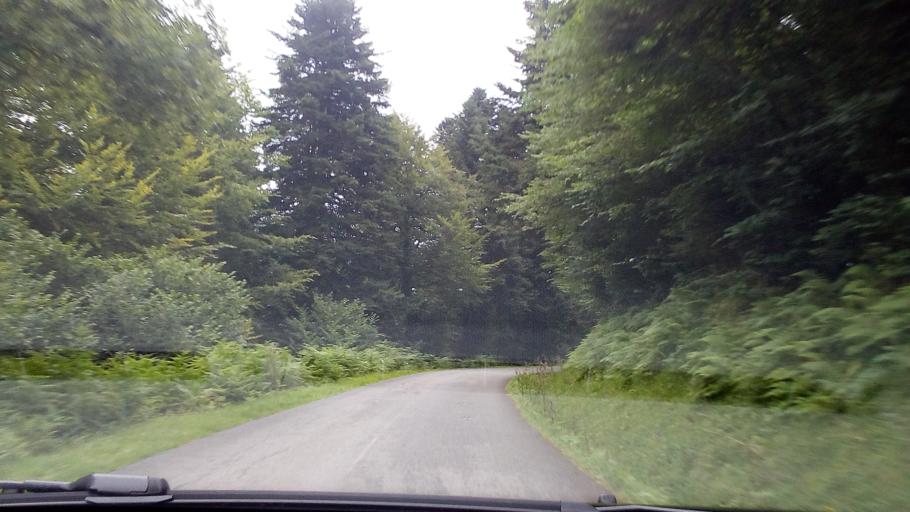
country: FR
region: Aquitaine
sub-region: Departement des Pyrenees-Atlantiques
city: Louvie-Juzon
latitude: 43.0651
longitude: -0.5000
